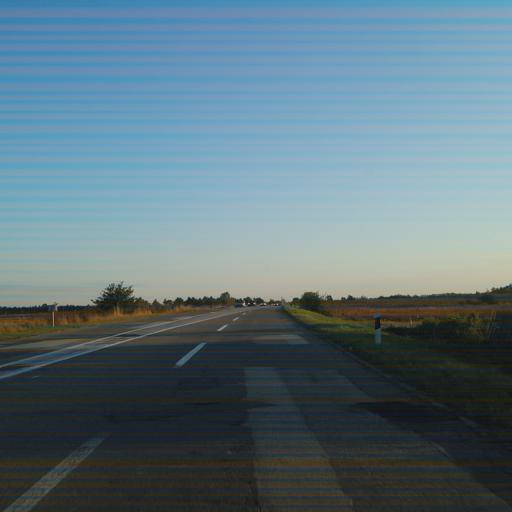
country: RS
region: Central Serbia
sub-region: Borski Okrug
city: Negotin
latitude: 44.1253
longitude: 22.3413
